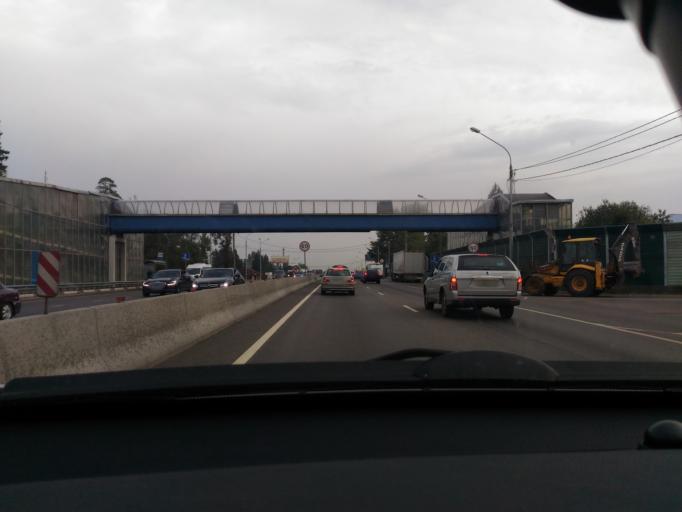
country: RU
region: Moskovskaya
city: Radumlya
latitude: 56.0763
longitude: 37.1271
